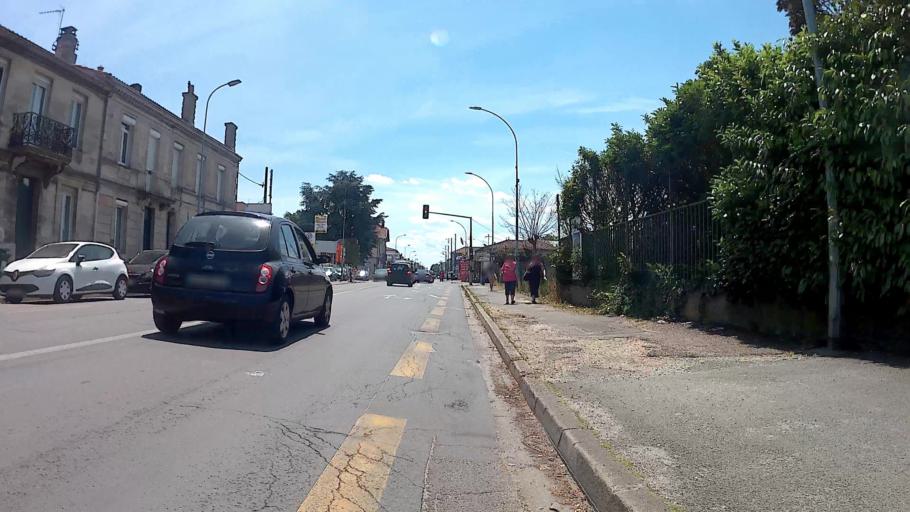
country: FR
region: Aquitaine
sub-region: Departement de la Gironde
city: Talence
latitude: 44.8135
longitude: -0.5779
